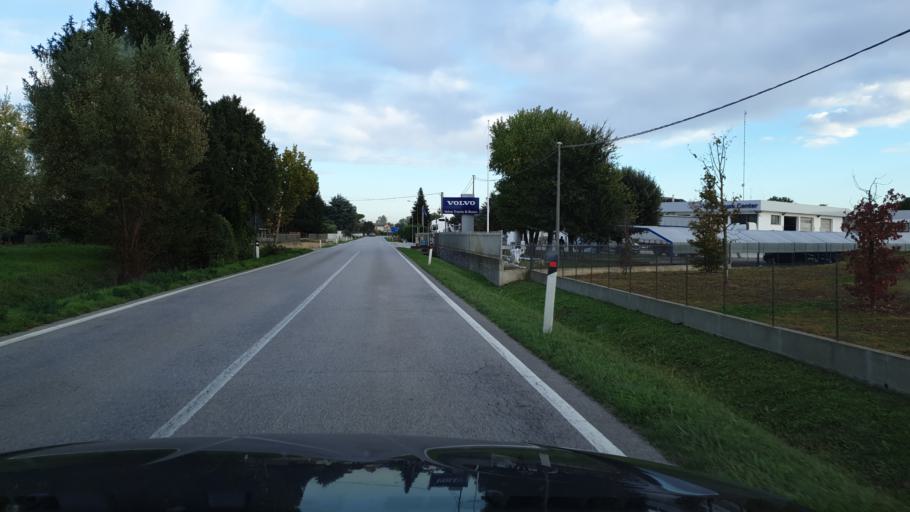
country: IT
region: Veneto
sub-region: Provincia di Padova
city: San Pietro Viminario
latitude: 45.2284
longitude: 11.8132
